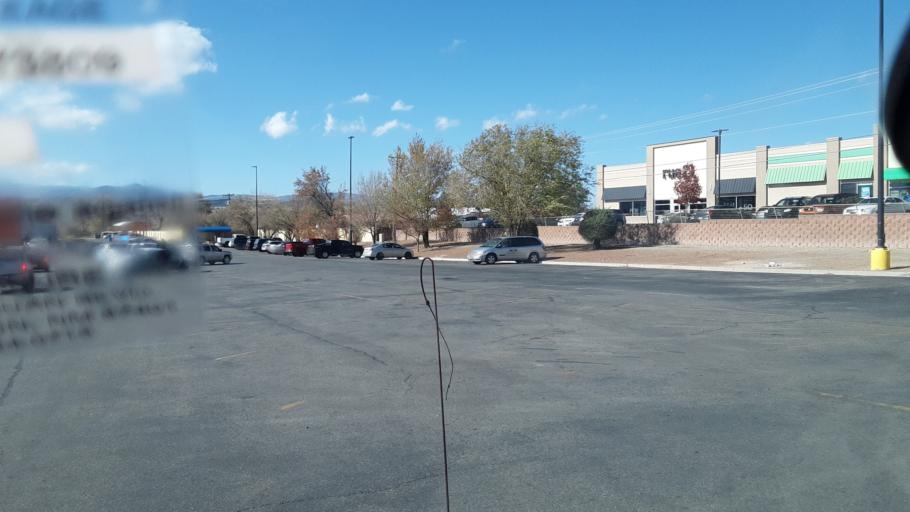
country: US
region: New Mexico
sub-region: Rio Arriba County
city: Espanola
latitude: 36.0160
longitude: -106.0655
